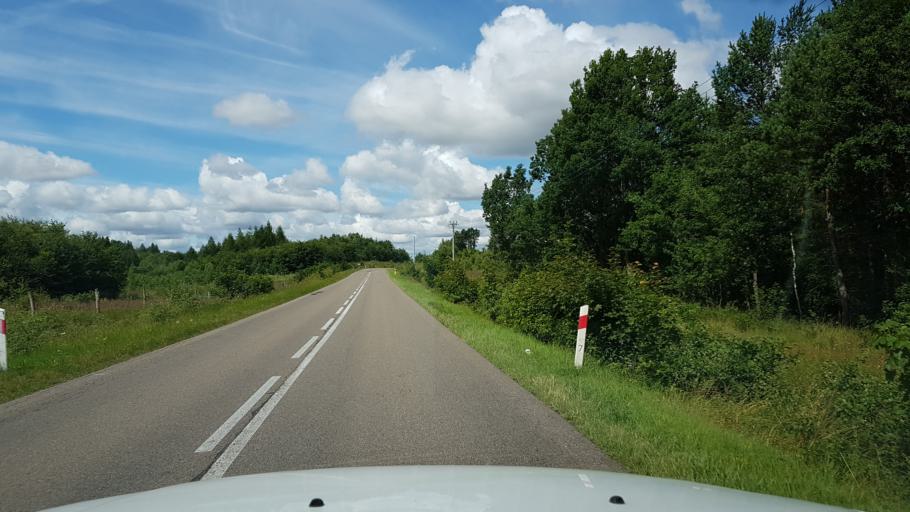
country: PL
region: West Pomeranian Voivodeship
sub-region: Powiat swidwinski
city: Rabino
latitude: 53.7775
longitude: 15.9289
